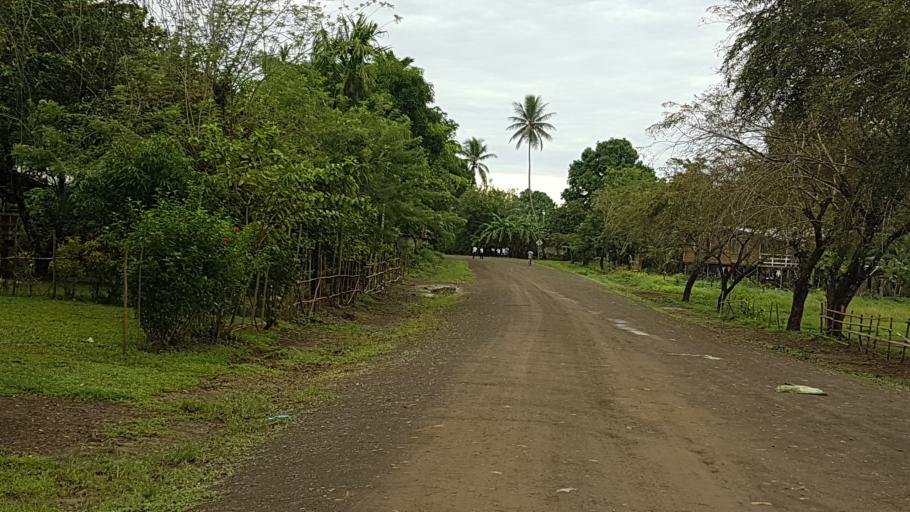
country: PG
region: Milne Bay
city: Alotau
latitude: -10.3197
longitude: 150.6806
